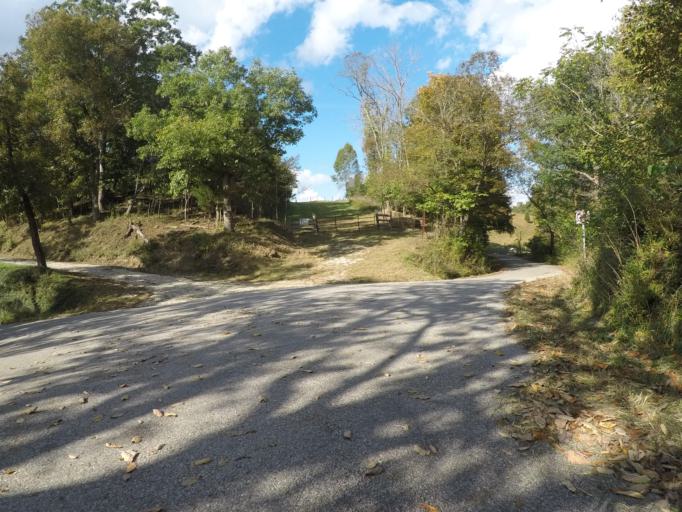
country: US
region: West Virginia
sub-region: Wayne County
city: Lavalette
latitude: 38.3682
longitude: -82.4749
